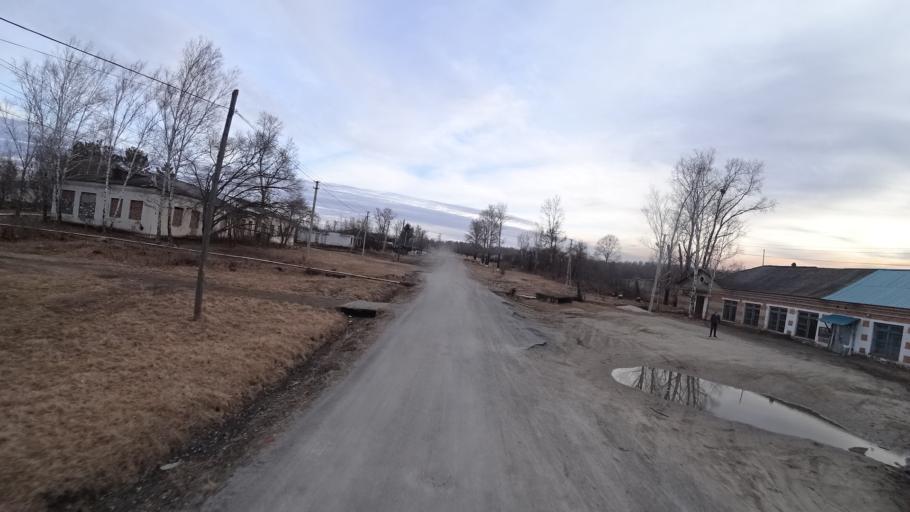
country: RU
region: Amur
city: Bureya
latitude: 50.0192
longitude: 129.7685
